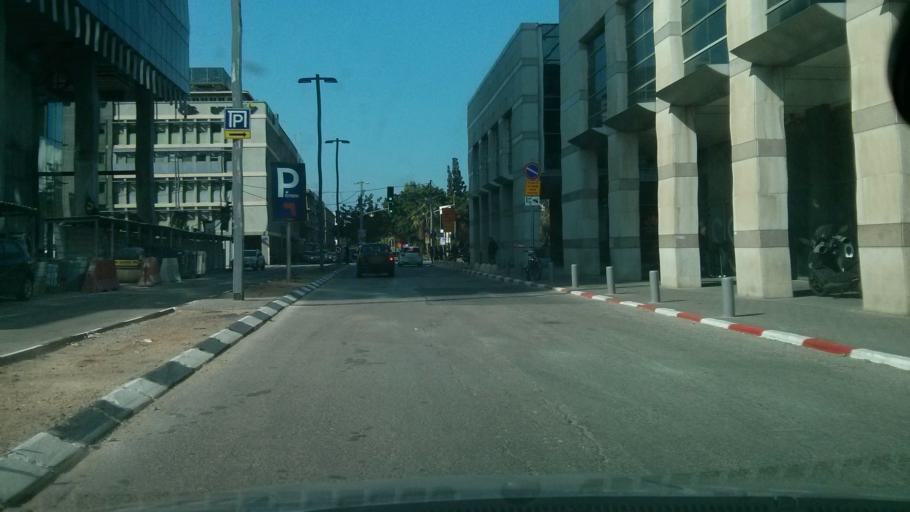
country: IL
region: Tel Aviv
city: Tel Aviv
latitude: 32.0704
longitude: 34.7871
